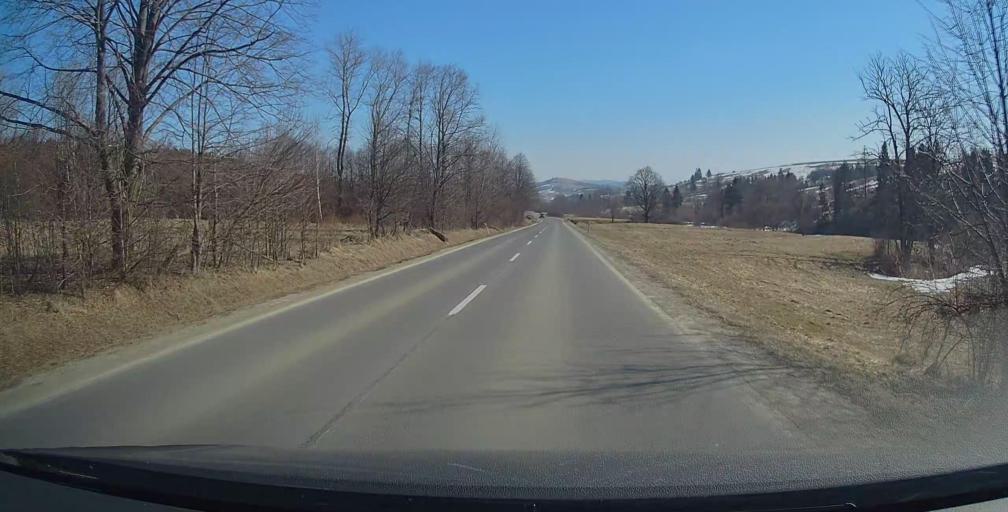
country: PL
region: Subcarpathian Voivodeship
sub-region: Powiat bieszczadzki
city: Ustrzyki Dolne
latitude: 49.5133
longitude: 22.6108
